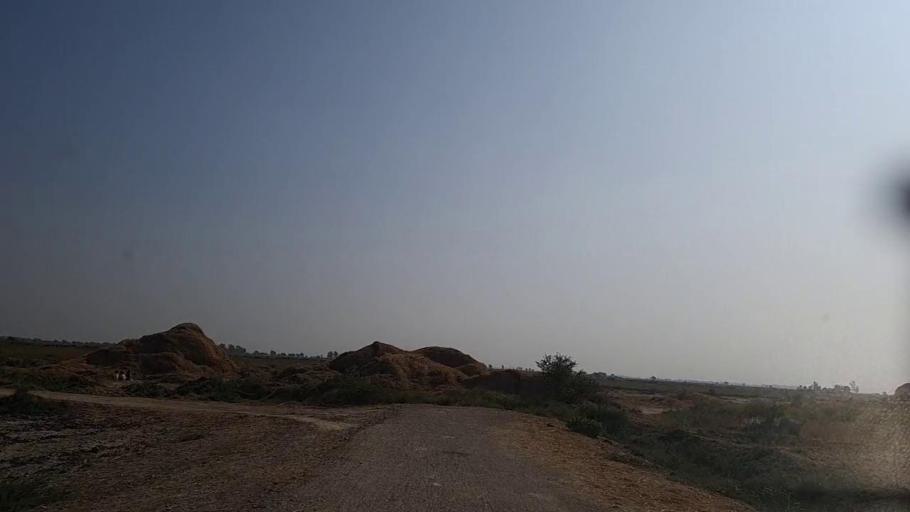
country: PK
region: Sindh
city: Mirpur Batoro
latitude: 24.5777
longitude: 68.2254
